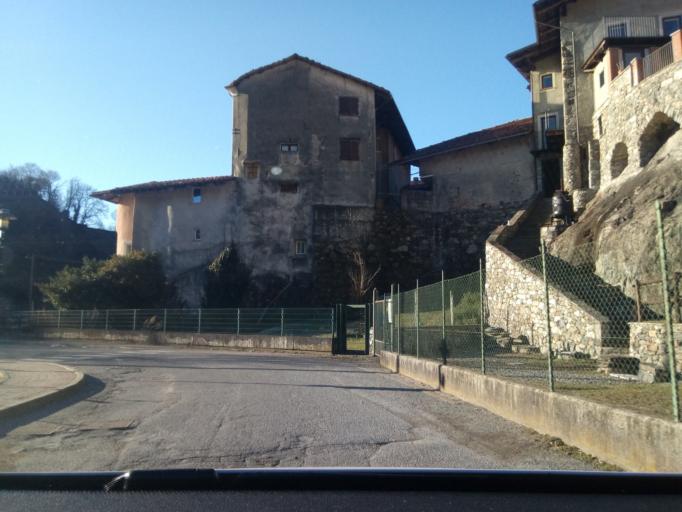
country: IT
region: Piedmont
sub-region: Provincia di Torino
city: Chiaverano
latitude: 45.4995
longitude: 7.9020
